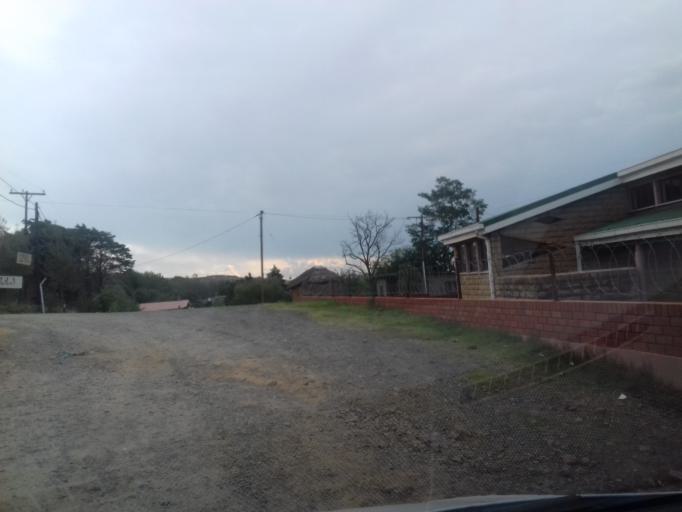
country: LS
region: Maseru
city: Nako
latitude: -29.6245
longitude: 27.5089
